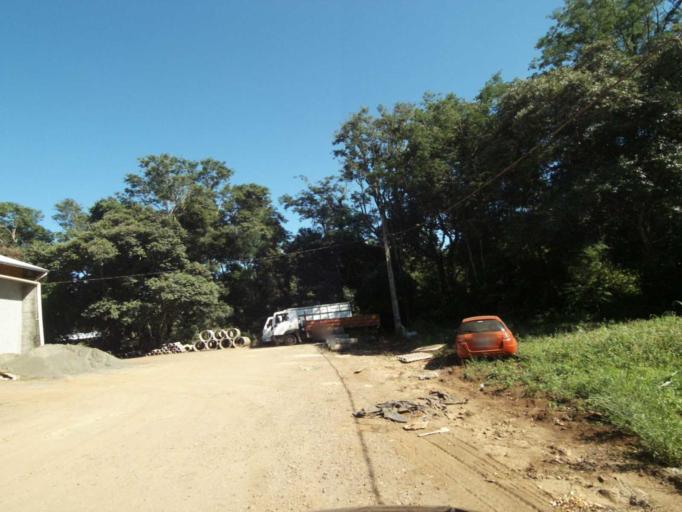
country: BR
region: Parana
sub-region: Francisco Beltrao
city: Francisco Beltrao
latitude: -26.1440
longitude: -53.3145
